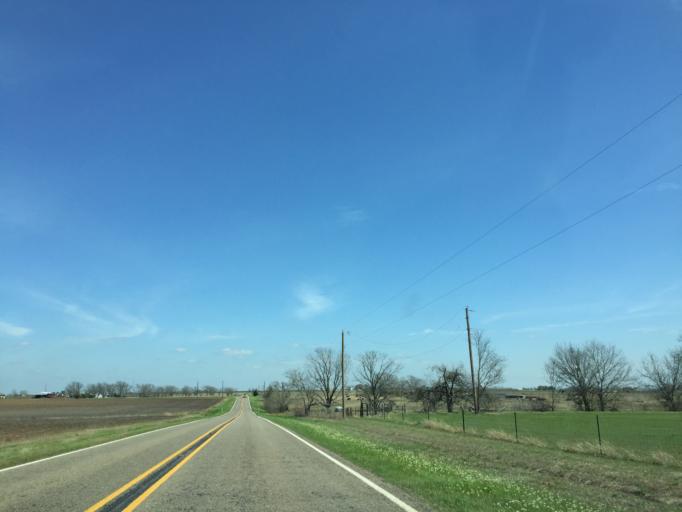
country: US
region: Texas
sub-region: Williamson County
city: Taylor
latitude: 30.5682
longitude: -97.3423
